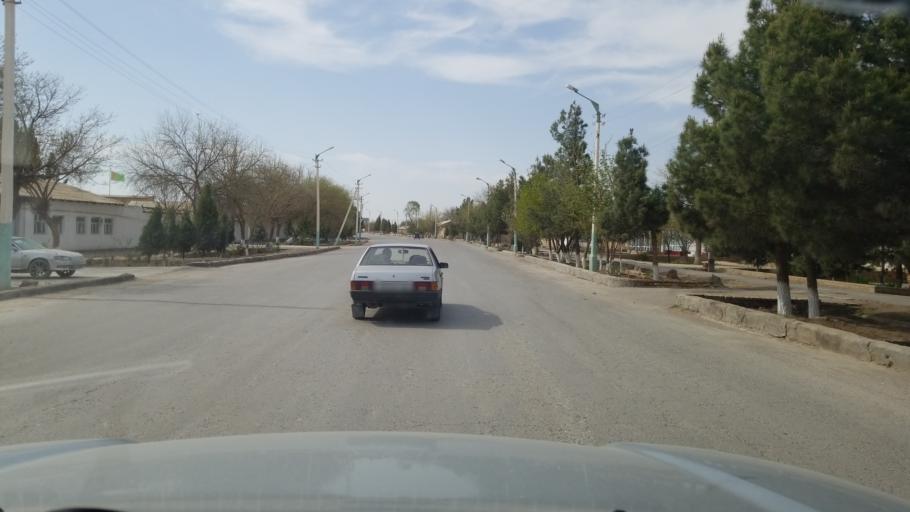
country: TM
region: Lebap
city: Atamyrat
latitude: 37.8436
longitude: 65.1987
